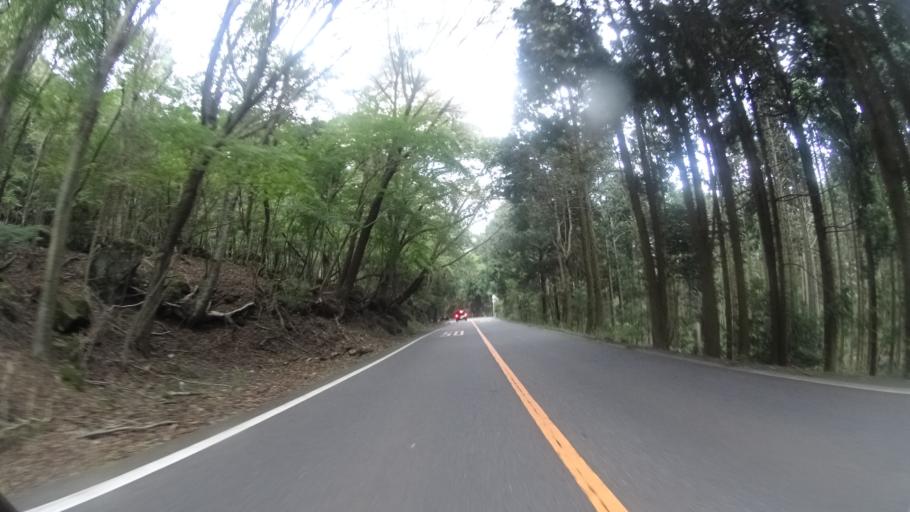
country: JP
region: Oita
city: Beppu
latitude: 33.2725
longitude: 131.4104
